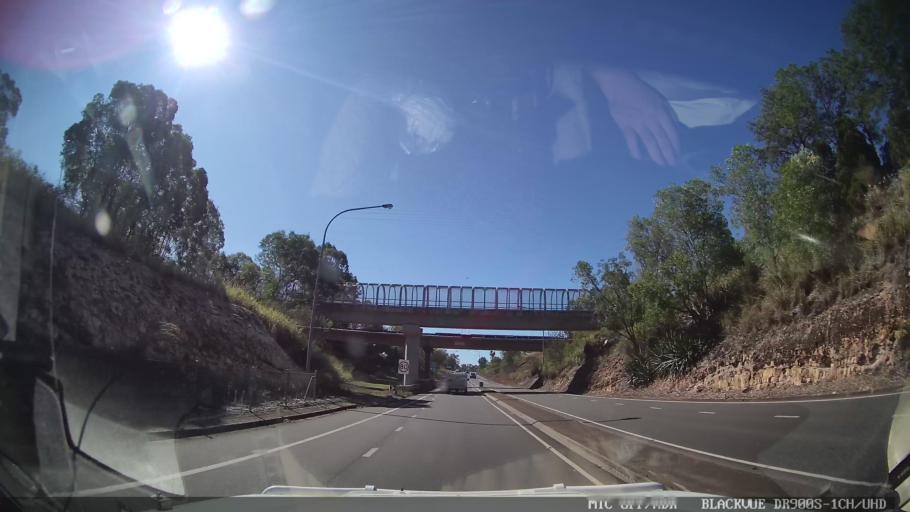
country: AU
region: Queensland
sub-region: Fraser Coast
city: Maryborough
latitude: -25.5179
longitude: 152.6696
